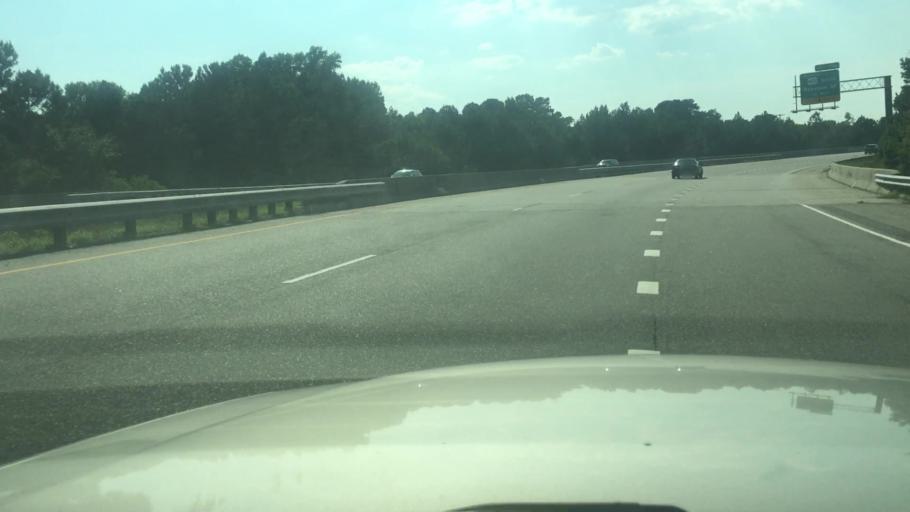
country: US
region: North Carolina
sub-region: Cumberland County
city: Fayetteville
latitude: 35.0389
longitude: -78.8891
